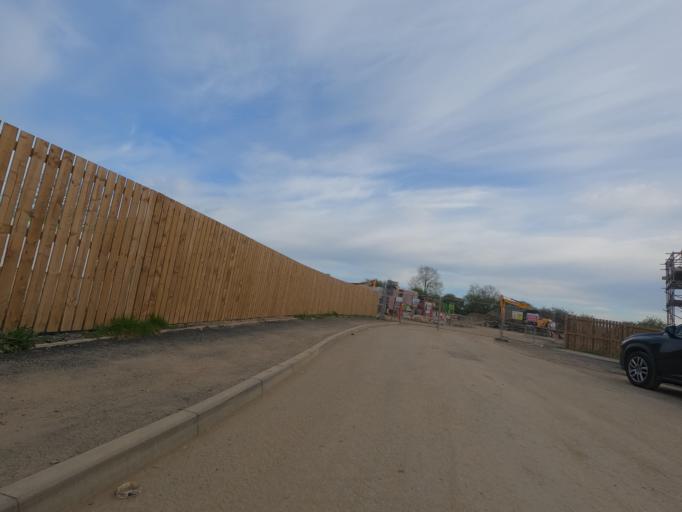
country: GB
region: England
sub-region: Newcastle upon Tyne
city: Dinnington
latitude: 55.0522
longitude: -1.6813
